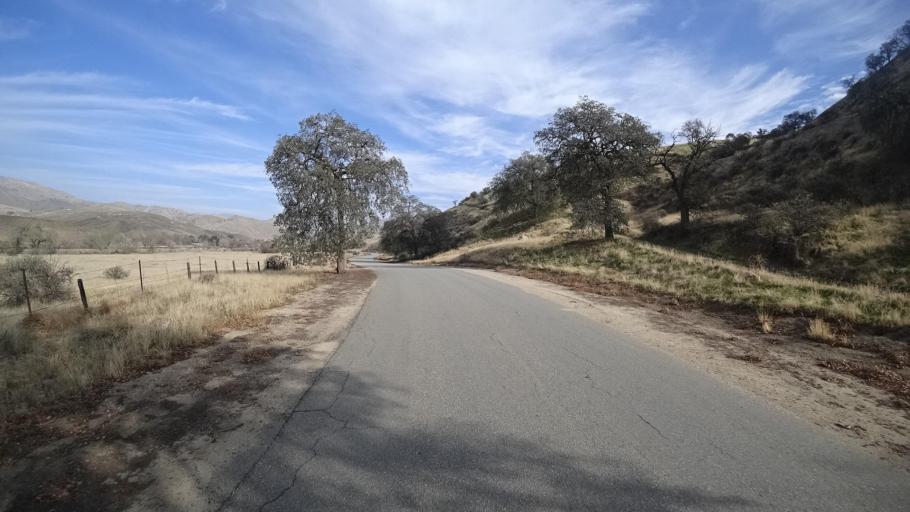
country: US
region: California
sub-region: Kern County
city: Bear Valley Springs
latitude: 35.2874
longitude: -118.6337
